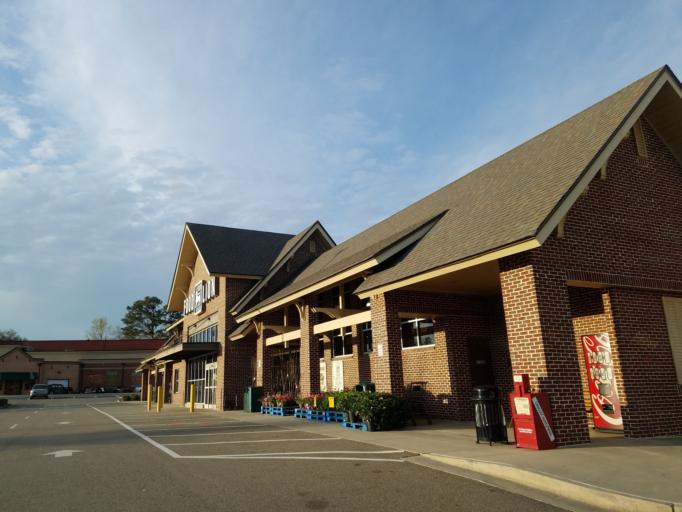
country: US
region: Georgia
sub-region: Dawson County
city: Dawsonville
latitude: 34.4171
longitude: -84.1118
